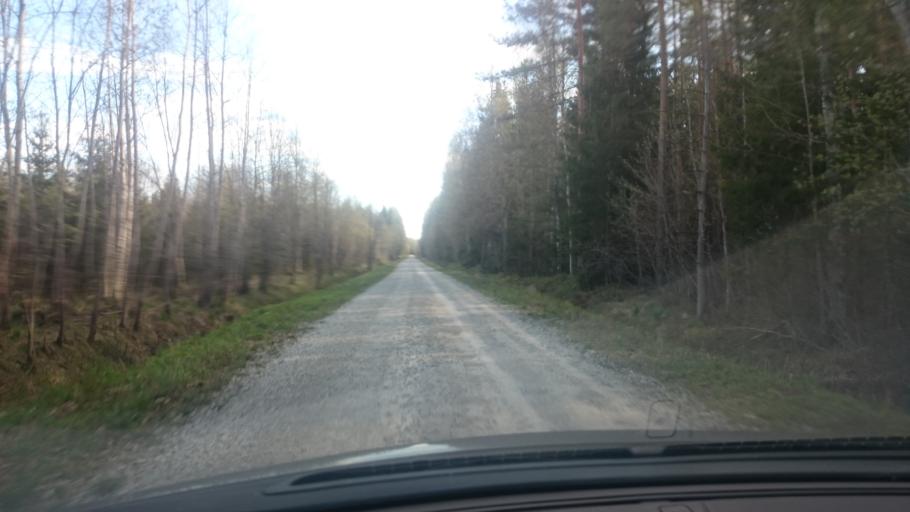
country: EE
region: Ida-Virumaa
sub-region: Sillamaee linn
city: Sillamae
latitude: 59.1574
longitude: 27.8013
